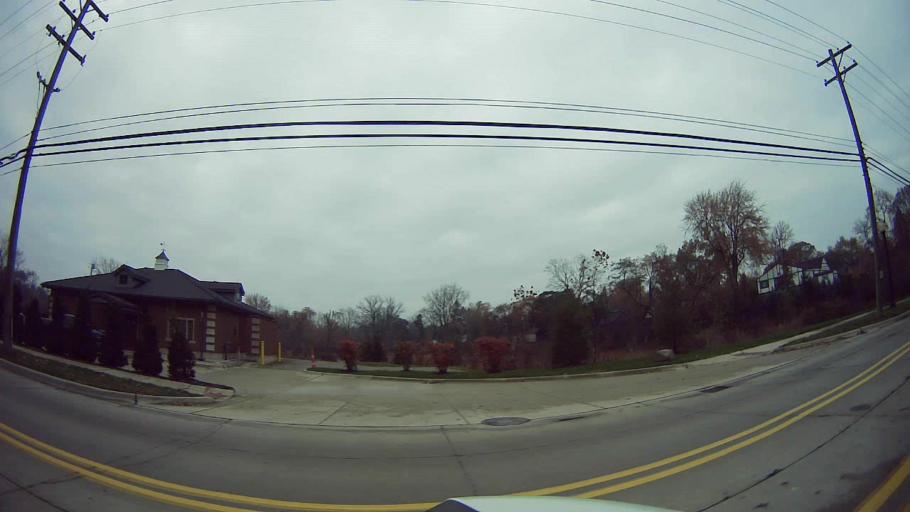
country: US
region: Michigan
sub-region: Wayne County
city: Dearborn Heights
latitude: 42.3092
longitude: -83.2529
